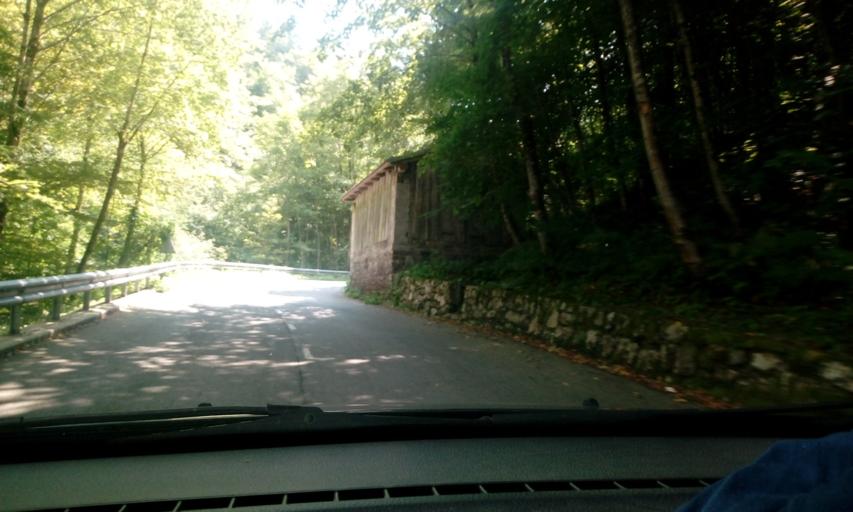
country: SI
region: Kobarid
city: Kobarid
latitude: 46.2194
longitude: 13.5904
